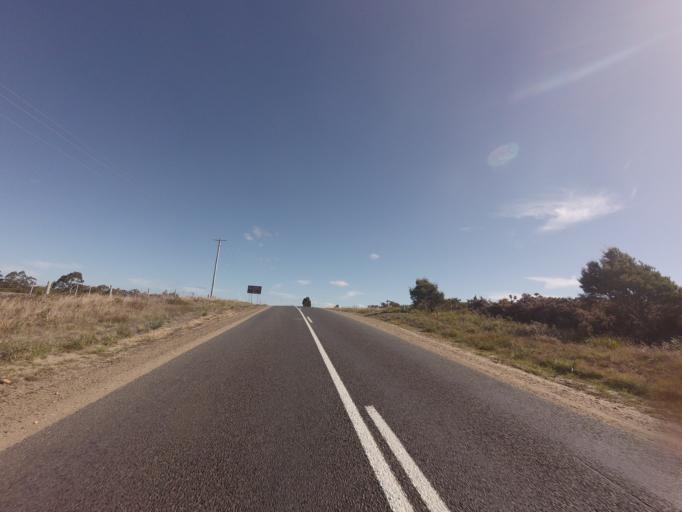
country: AU
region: Tasmania
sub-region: Break O'Day
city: St Helens
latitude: -41.9385
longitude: 148.2212
